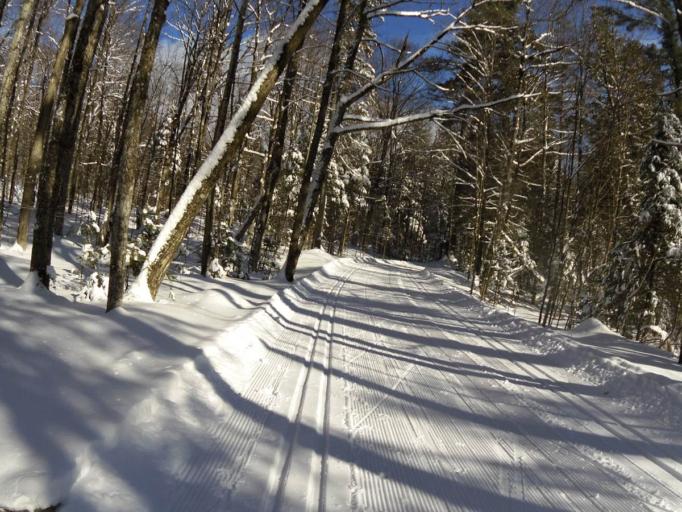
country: CA
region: Quebec
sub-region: Outaouais
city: Wakefield
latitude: 45.5672
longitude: -75.9092
